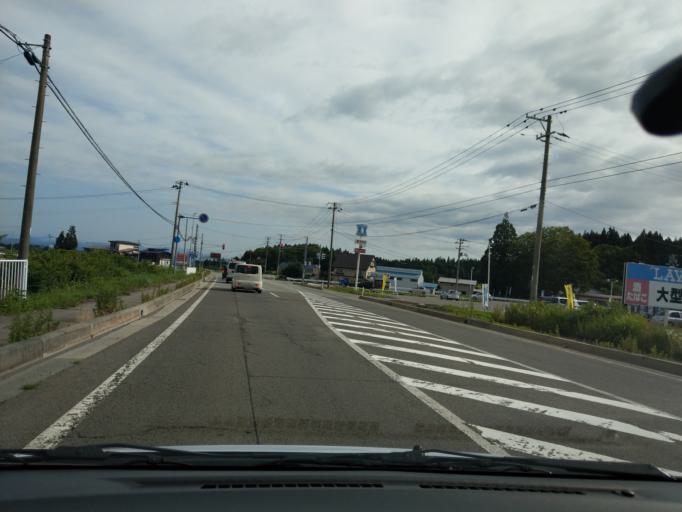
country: JP
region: Akita
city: Yokotemachi
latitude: 39.3805
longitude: 140.5681
